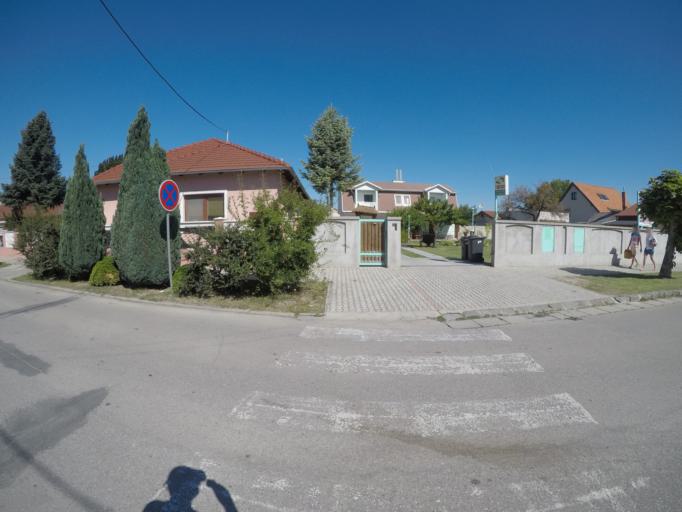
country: SK
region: Trnavsky
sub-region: Okres Dunajska Streda
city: Velky Meder
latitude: 47.8511
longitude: 17.7655
